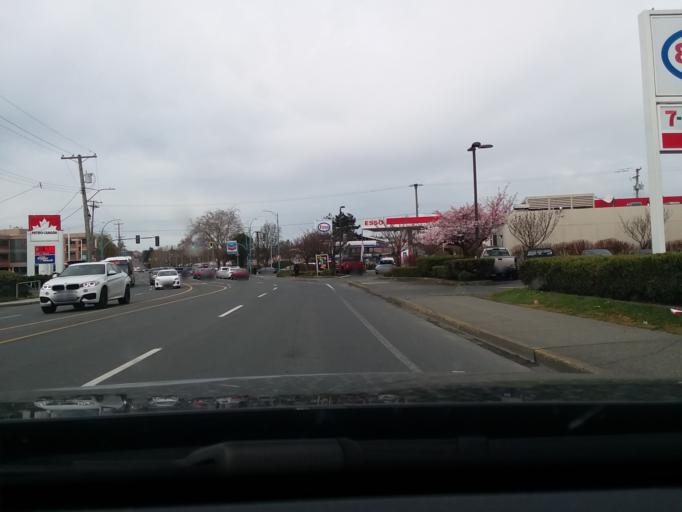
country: CA
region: British Columbia
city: Oak Bay
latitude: 48.4461
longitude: -123.3320
